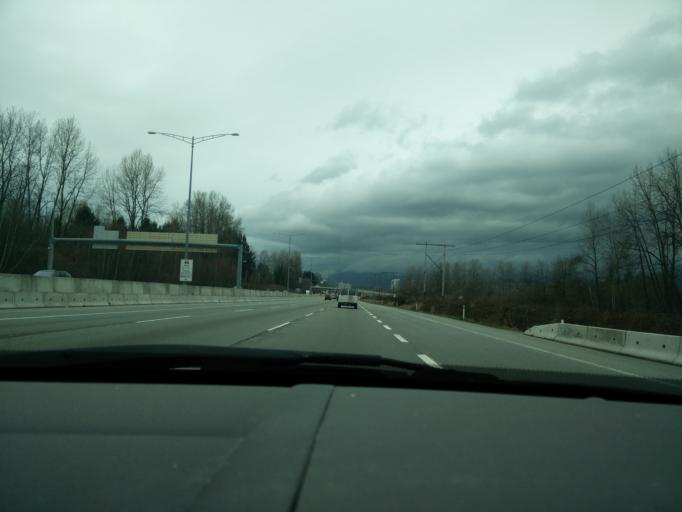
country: CA
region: British Columbia
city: Burnaby
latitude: 49.2454
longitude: -122.9691
